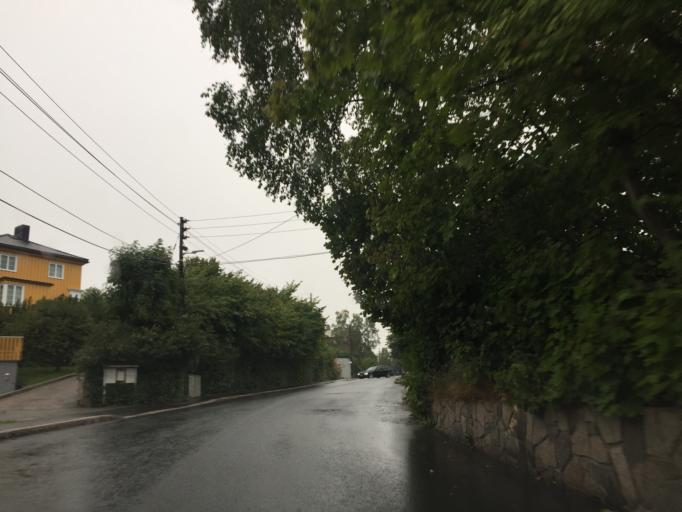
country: NO
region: Oslo
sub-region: Oslo
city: Sjolyststranda
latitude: 59.9486
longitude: 10.6960
